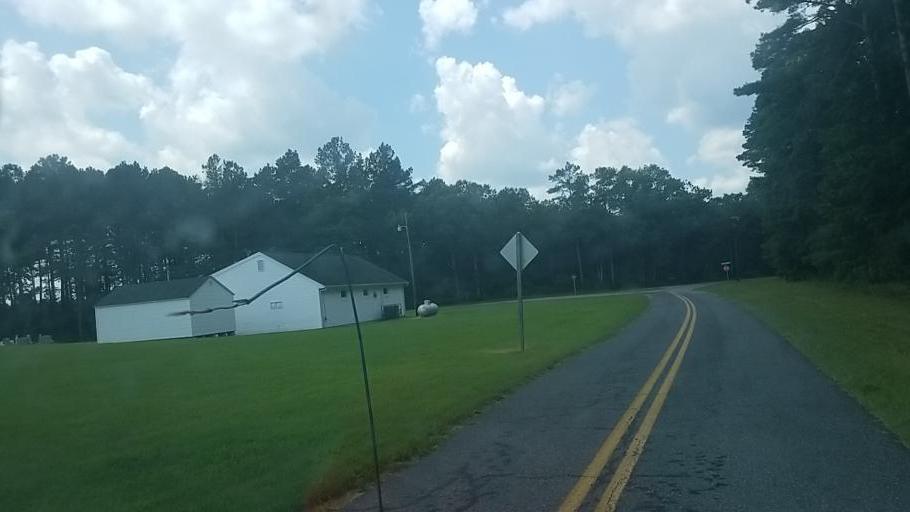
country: US
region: Maryland
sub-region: Worcester County
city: Snow Hill
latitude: 38.2561
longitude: -75.4428
